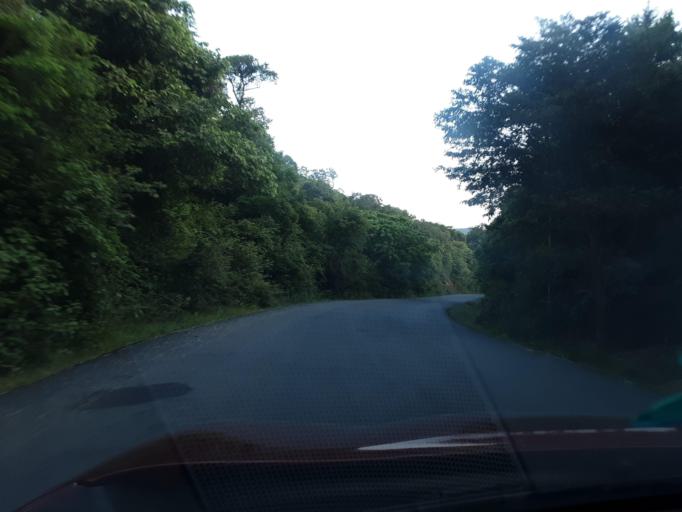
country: LK
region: Central
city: Dambulla
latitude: 7.8139
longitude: 80.7665
